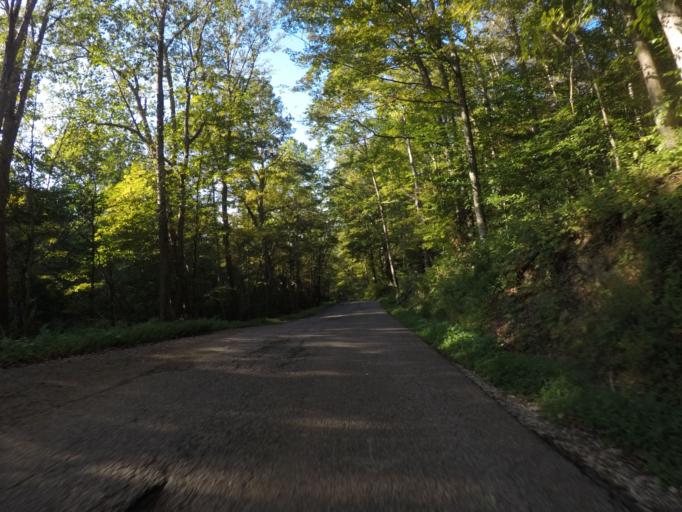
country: US
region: Kentucky
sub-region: Boyd County
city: Ashland
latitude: 38.5270
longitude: -82.5331
